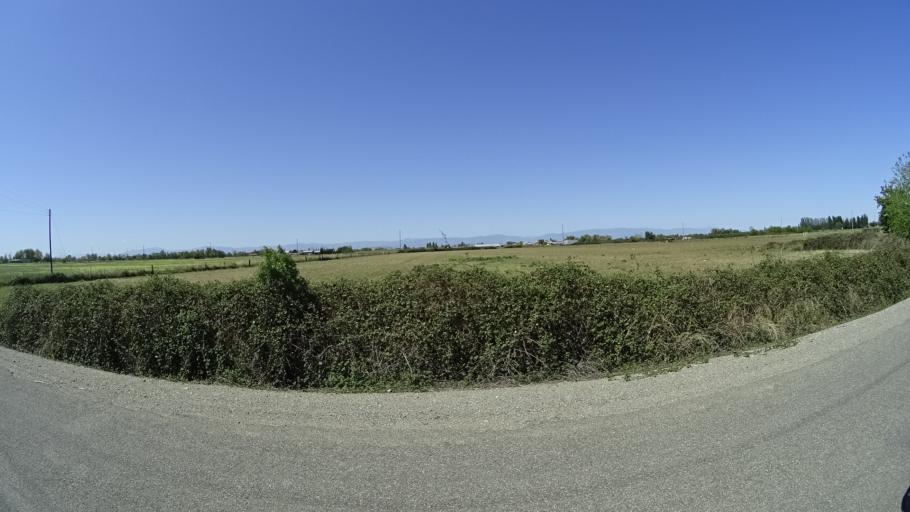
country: US
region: California
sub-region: Glenn County
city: Orland
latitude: 39.7727
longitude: -122.1408
